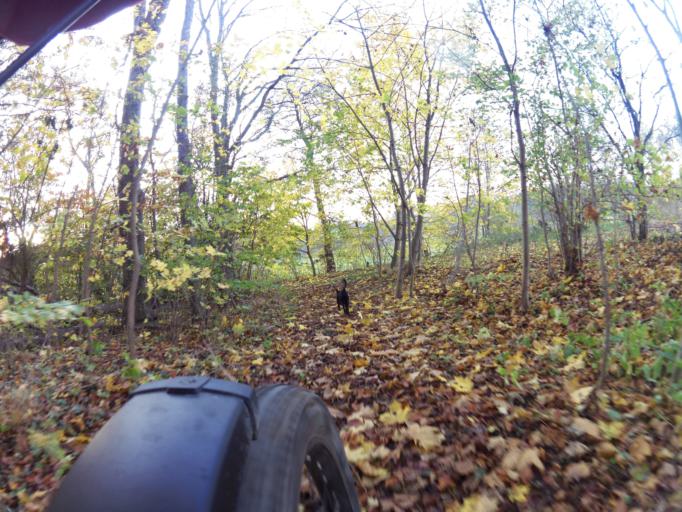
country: PL
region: Pomeranian Voivodeship
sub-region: Powiat pucki
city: Krokowa
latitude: 54.7724
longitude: 18.1706
